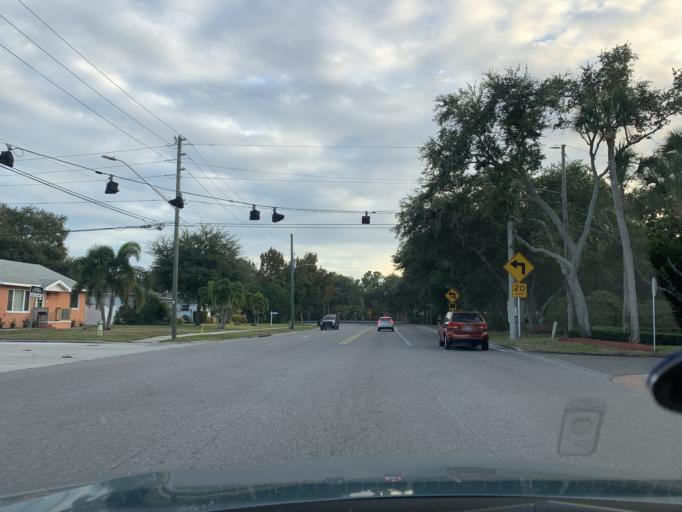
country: US
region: Florida
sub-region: Pinellas County
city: South Pasadena
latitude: 27.7775
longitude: -82.7457
